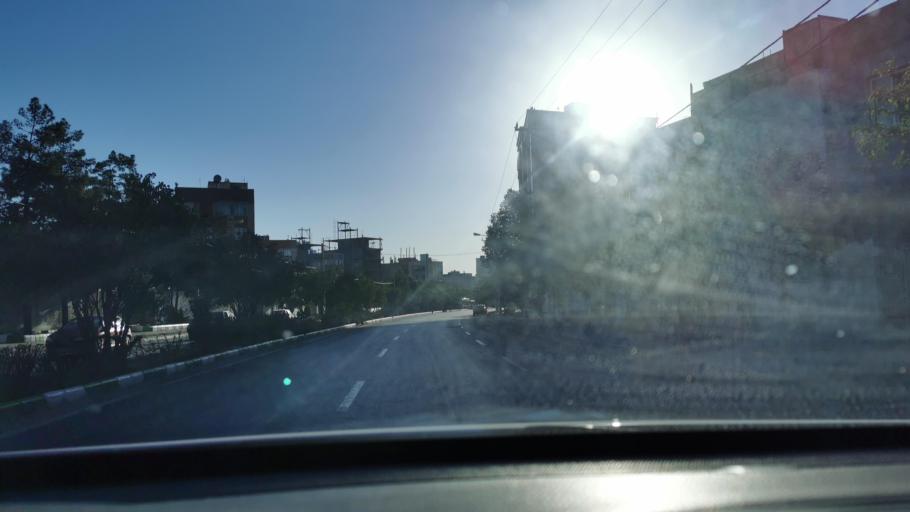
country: IR
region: Razavi Khorasan
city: Mashhad
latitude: 36.3507
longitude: 59.4802
